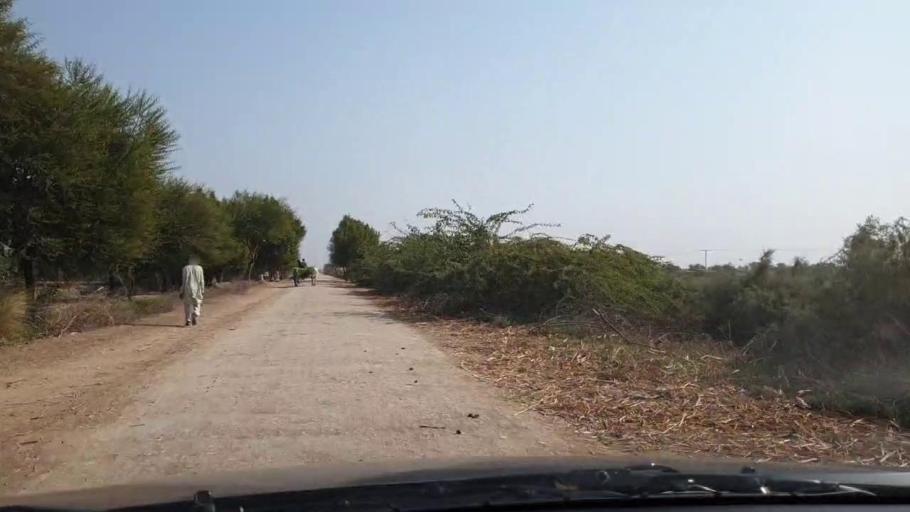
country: PK
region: Sindh
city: Jhol
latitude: 25.9972
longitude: 68.9166
